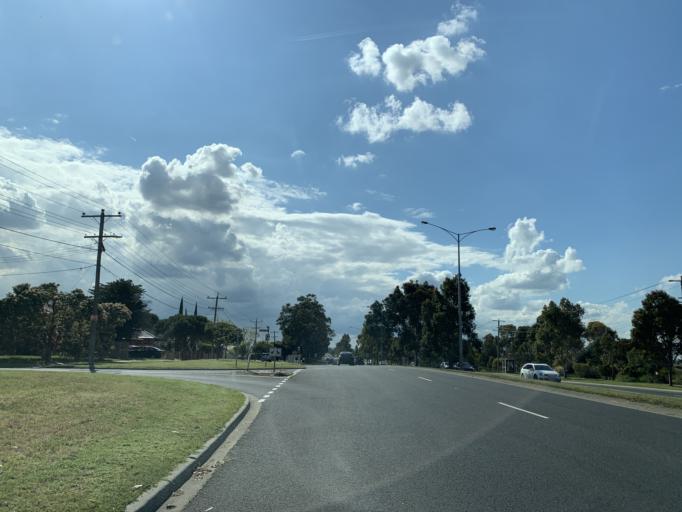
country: AU
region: Victoria
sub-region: Brimbank
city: Kealba
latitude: -37.7440
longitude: 144.8272
